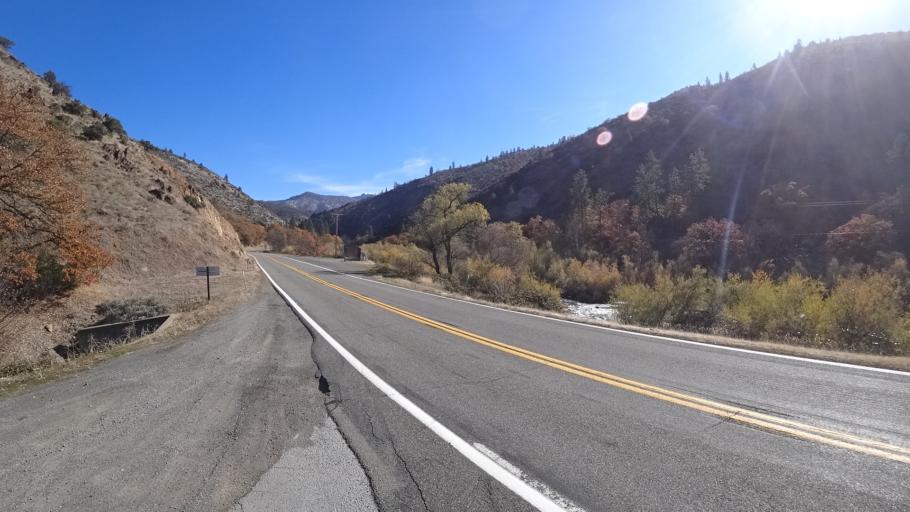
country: US
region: California
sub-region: Siskiyou County
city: Yreka
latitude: 41.8340
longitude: -122.6200
